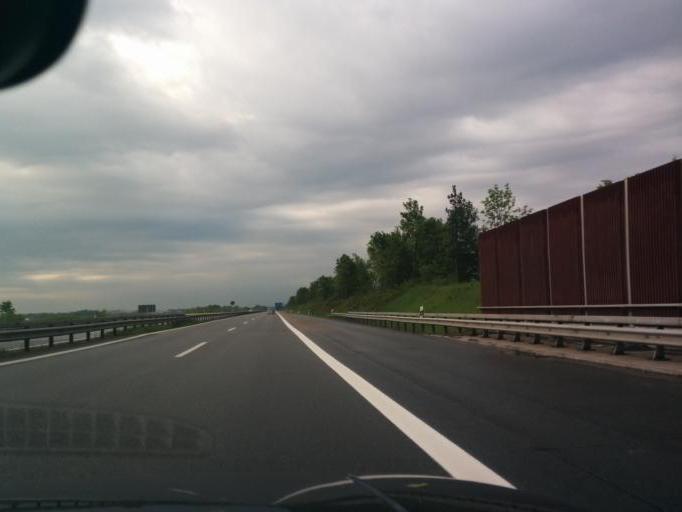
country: DE
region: Bavaria
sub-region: Upper Bavaria
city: Unterhaching
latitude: 48.0666
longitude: 11.6320
